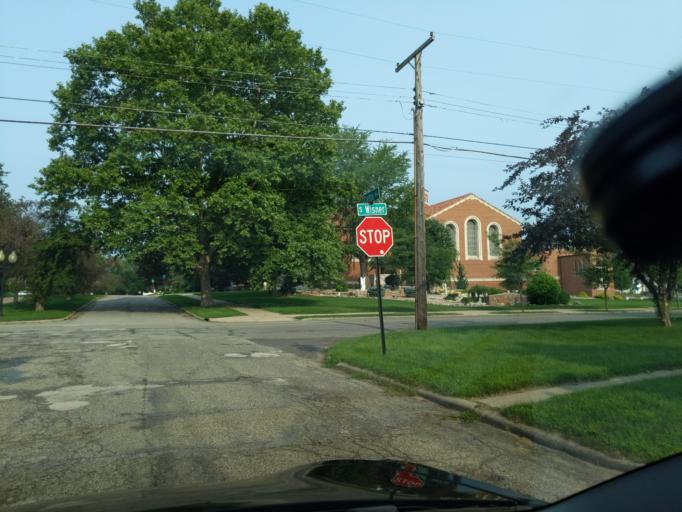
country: US
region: Michigan
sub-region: Jackson County
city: Jackson
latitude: 42.2421
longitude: -84.4285
